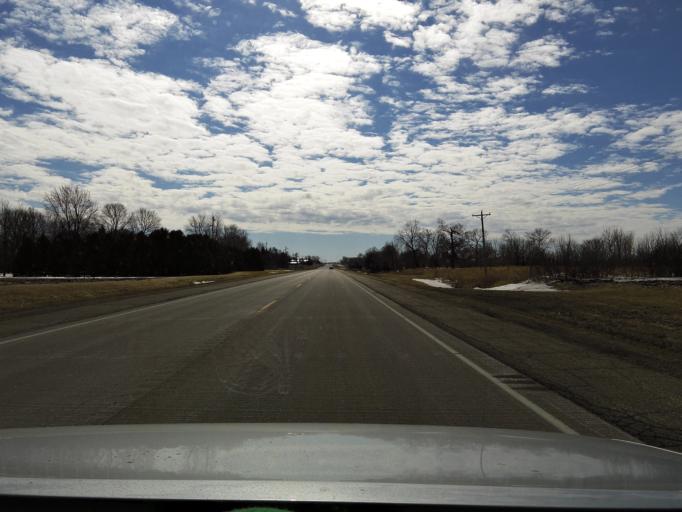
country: US
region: Minnesota
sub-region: Le Sueur County
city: New Prague
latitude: 44.5037
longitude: -93.5856
